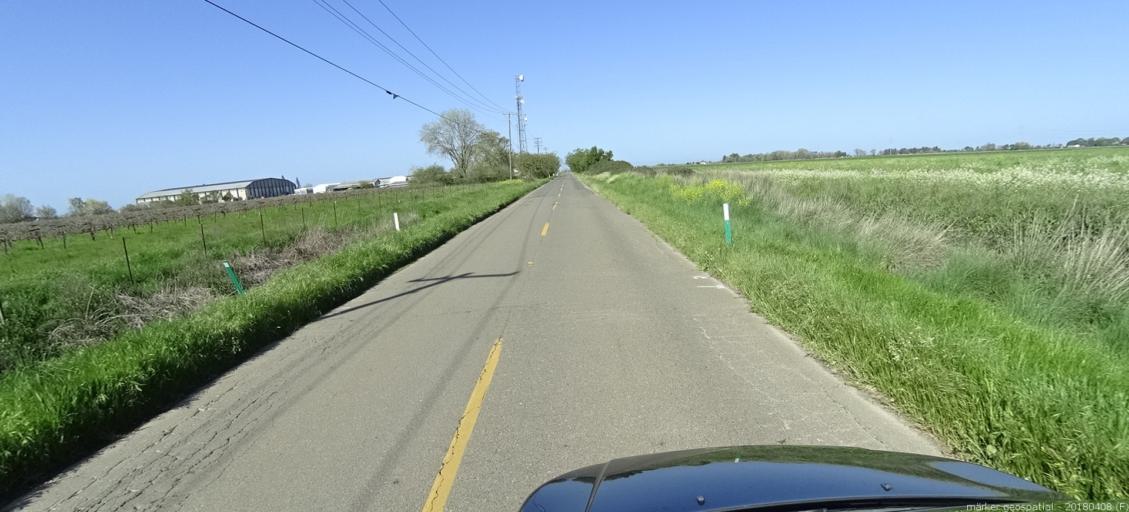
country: US
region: California
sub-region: Sacramento County
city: Elk Grove
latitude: 38.3507
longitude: -121.3929
